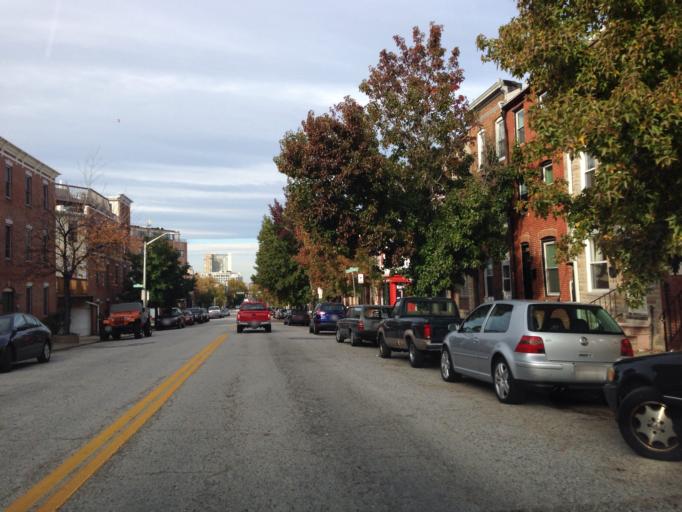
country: US
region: Maryland
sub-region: City of Baltimore
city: Baltimore
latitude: 39.2849
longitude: -76.5845
